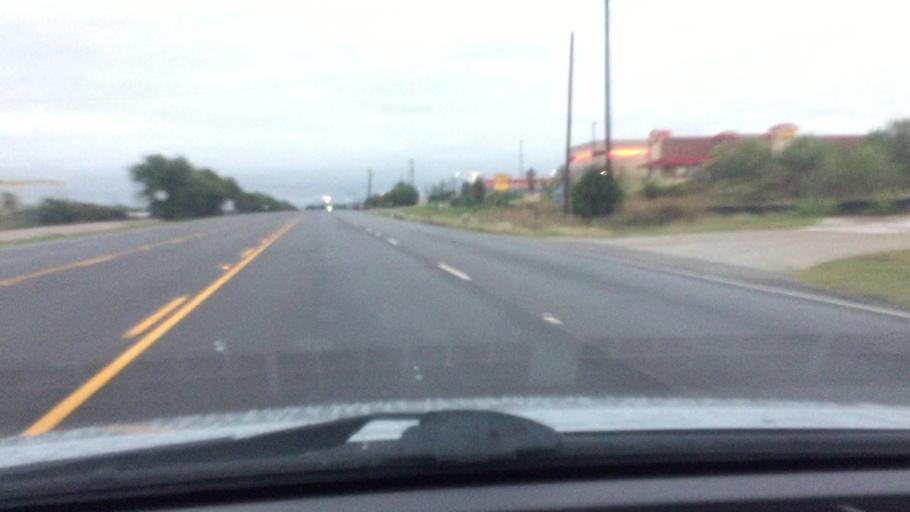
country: US
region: Texas
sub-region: Williamson County
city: Leander
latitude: 30.5655
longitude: -97.8474
